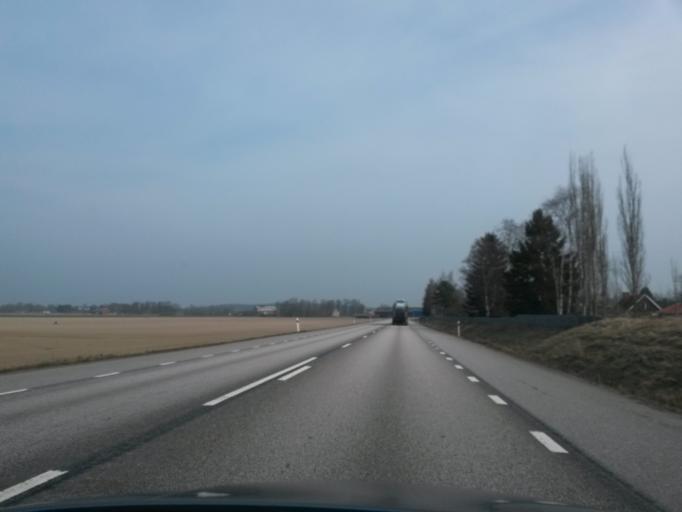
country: SE
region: Vaestra Goetaland
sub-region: Gullspangs Kommun
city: Hova
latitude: 58.8558
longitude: 14.2077
